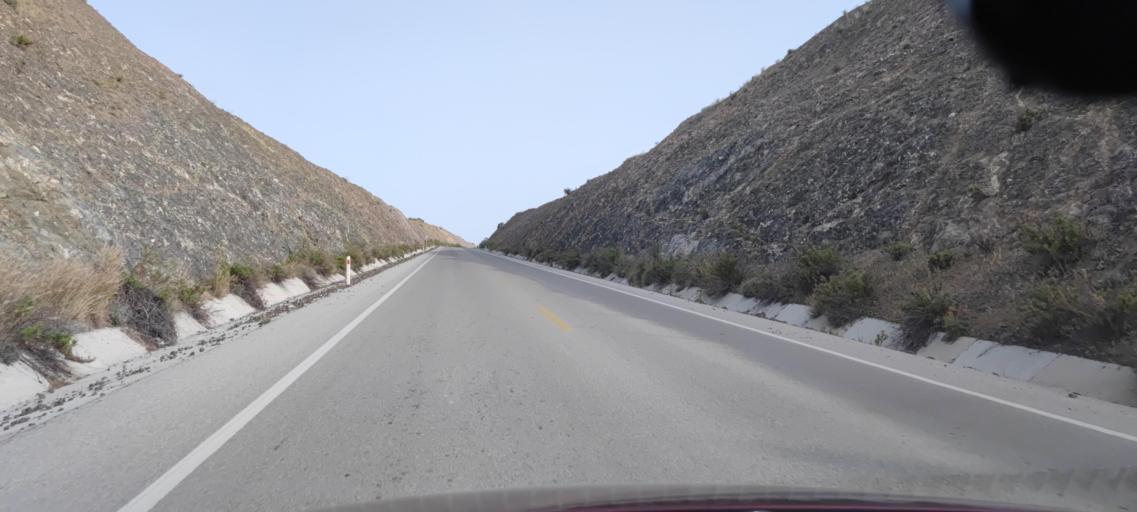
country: CY
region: Ammochostos
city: Leonarisso
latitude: 35.4883
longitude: 34.1005
